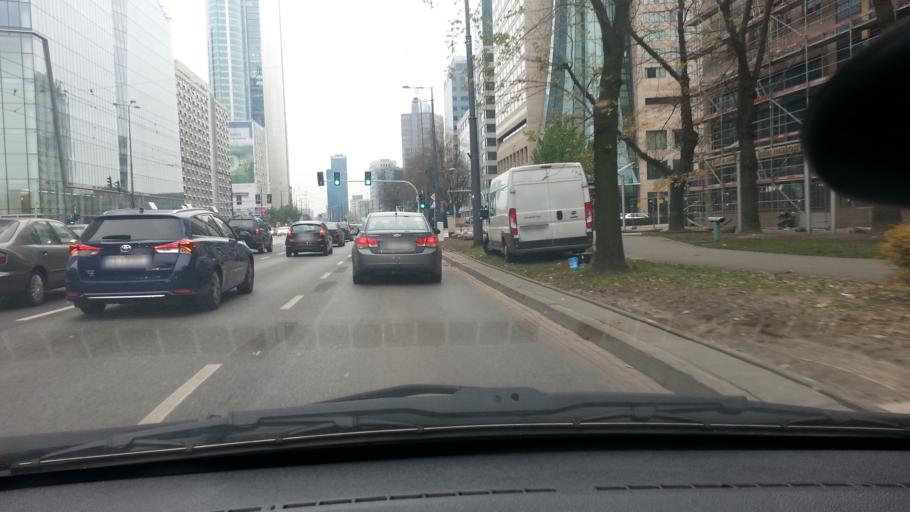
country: PL
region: Masovian Voivodeship
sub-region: Warszawa
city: Wola
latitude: 52.2367
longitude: 20.9967
